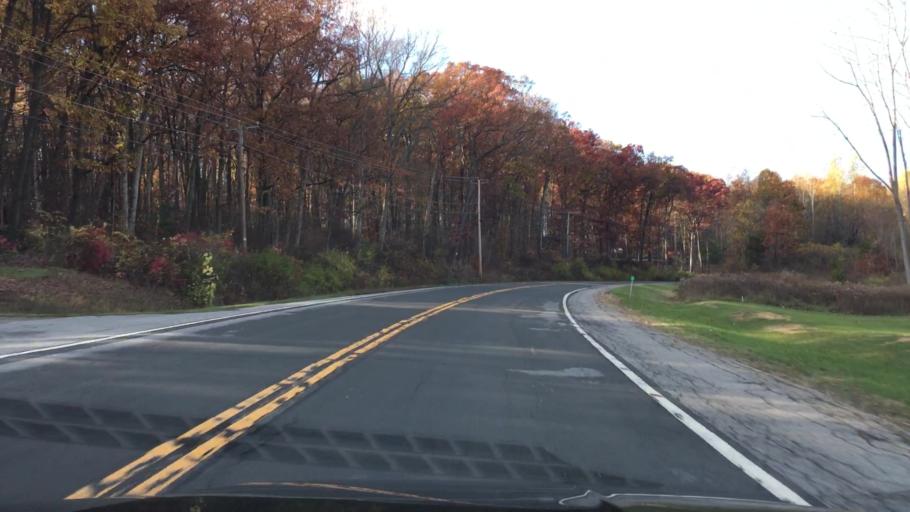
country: US
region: New York
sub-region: Dutchess County
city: Myers Corner
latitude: 41.6078
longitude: -73.8472
